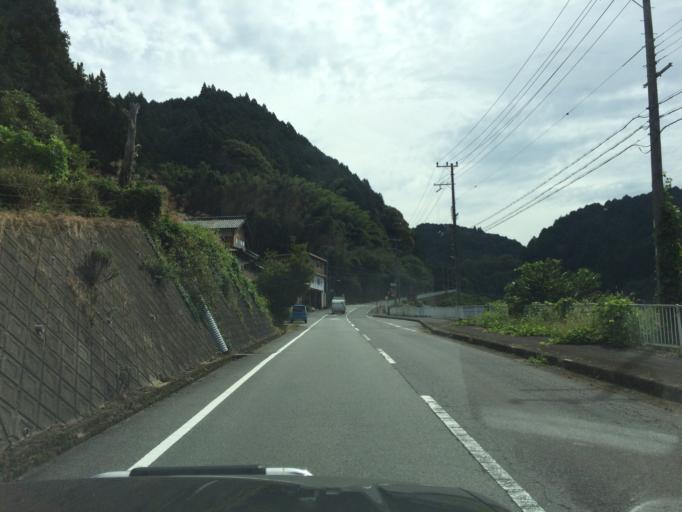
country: JP
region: Mie
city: Nabari
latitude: 34.6794
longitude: 135.9794
